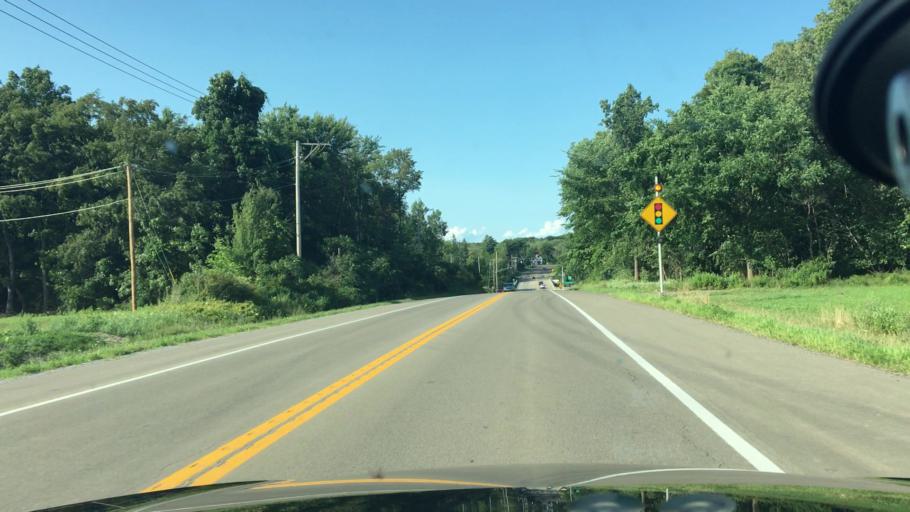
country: US
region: New York
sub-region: Erie County
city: Eden
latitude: 42.6924
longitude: -78.9384
